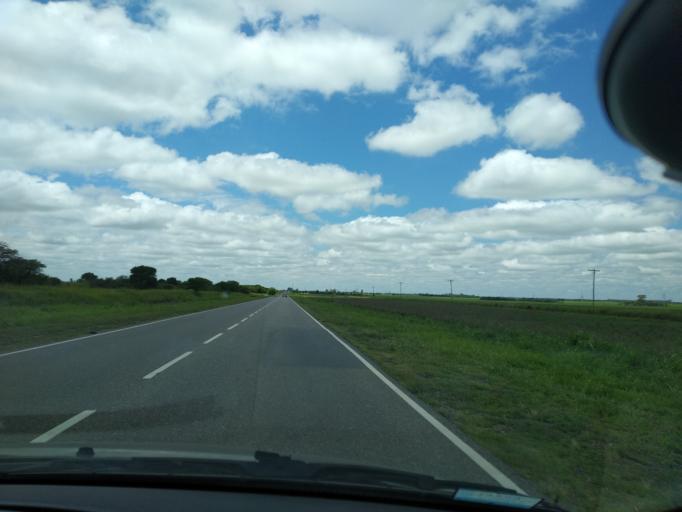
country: AR
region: Cordoba
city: Toledo
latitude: -31.6490
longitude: -64.1227
